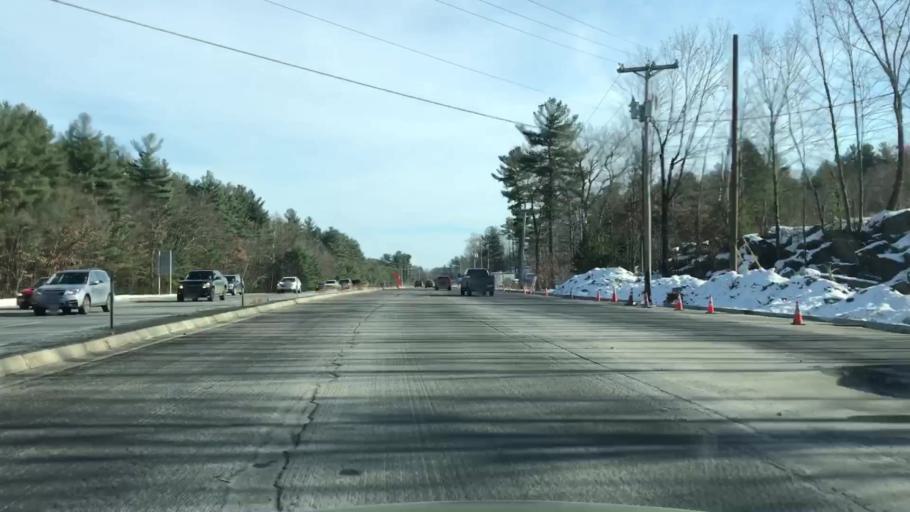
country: US
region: New Hampshire
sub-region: Hillsborough County
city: Milford
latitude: 42.8244
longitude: -71.6140
